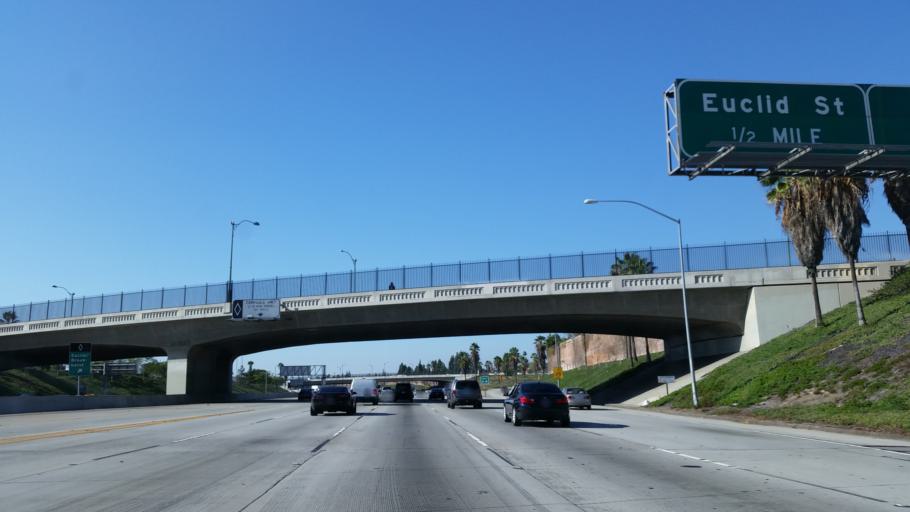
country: US
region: California
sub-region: Orange County
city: Anaheim
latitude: 33.8291
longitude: -117.9283
